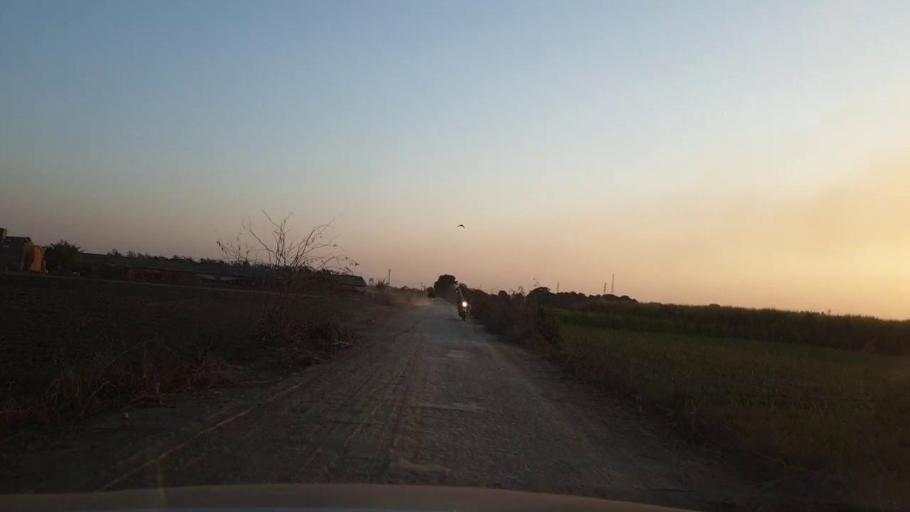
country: PK
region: Sindh
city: Tando Allahyar
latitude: 25.5281
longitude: 68.6248
